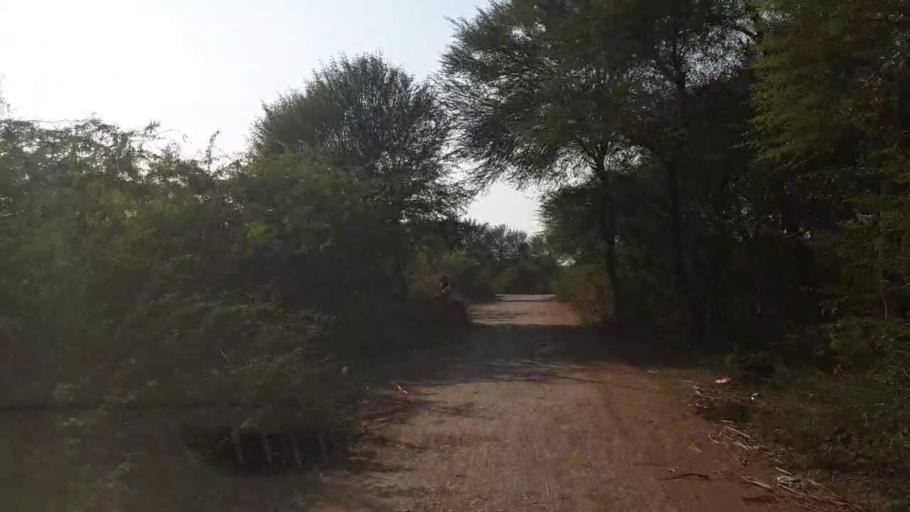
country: PK
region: Sindh
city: Mirpur Khas
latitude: 25.4131
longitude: 68.9192
